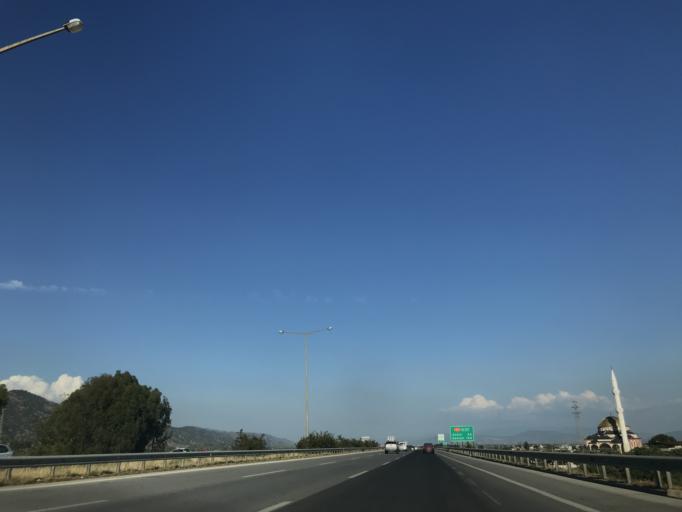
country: TR
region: Aydin
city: Germencik
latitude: 37.8811
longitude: 27.5900
